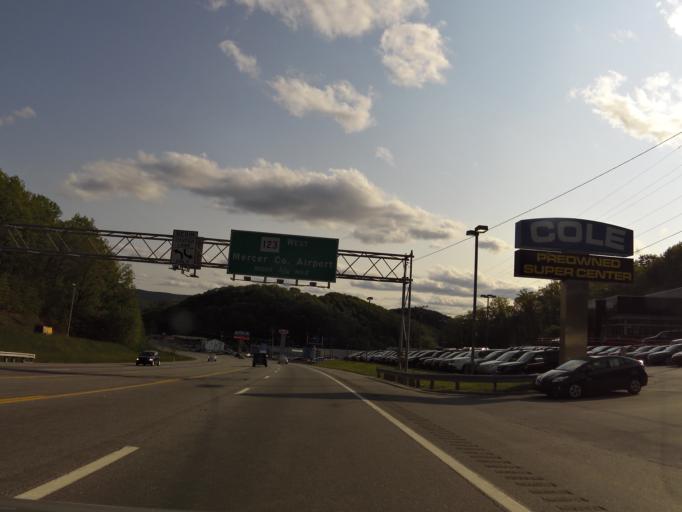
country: US
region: West Virginia
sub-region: Mercer County
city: Princeton
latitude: 37.3253
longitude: -81.1335
